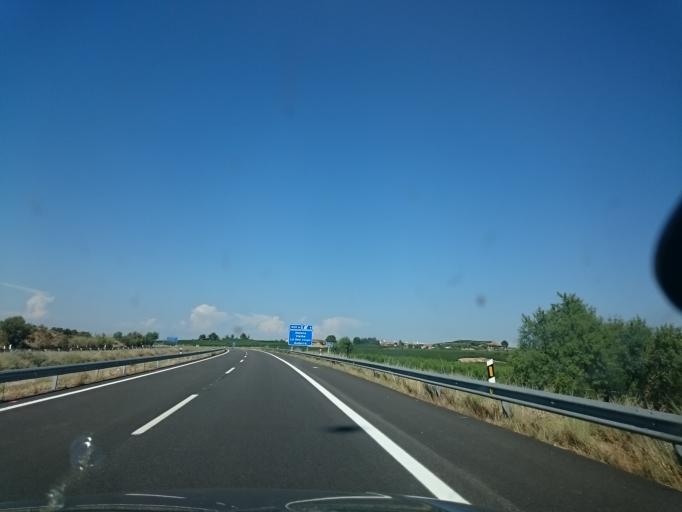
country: ES
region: Catalonia
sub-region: Provincia de Lleida
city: Soses
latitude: 41.5219
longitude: 0.4637
